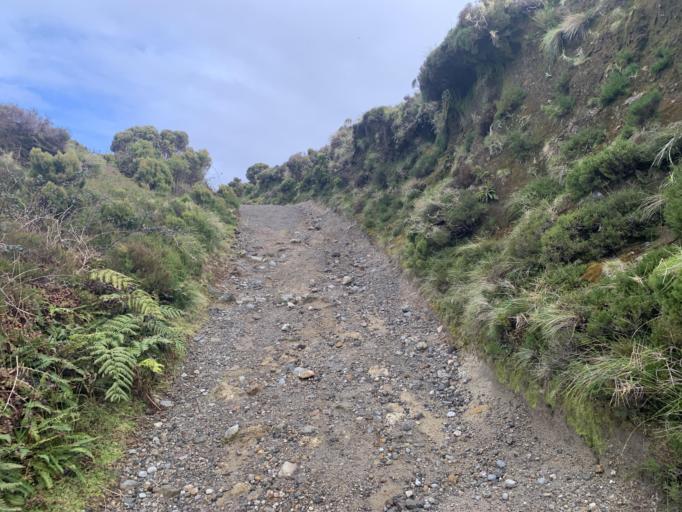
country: PT
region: Azores
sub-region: Vila Franca do Campo
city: Vila Franca do Campo
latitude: 37.7602
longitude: -25.4805
